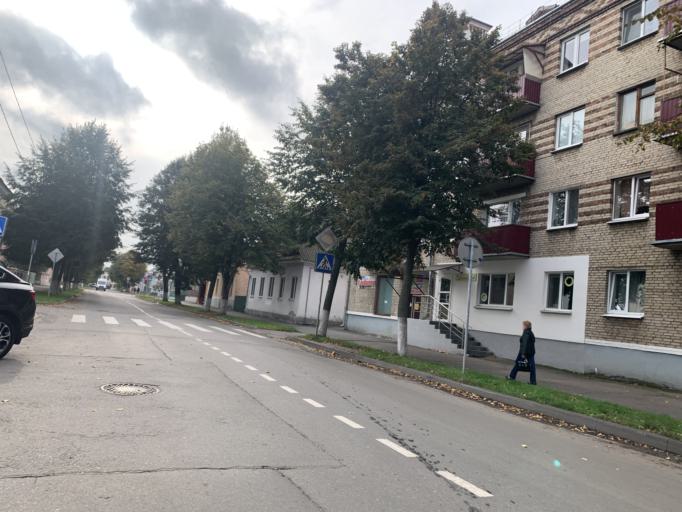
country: BY
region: Brest
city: Pinsk
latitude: 52.1172
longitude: 26.1118
